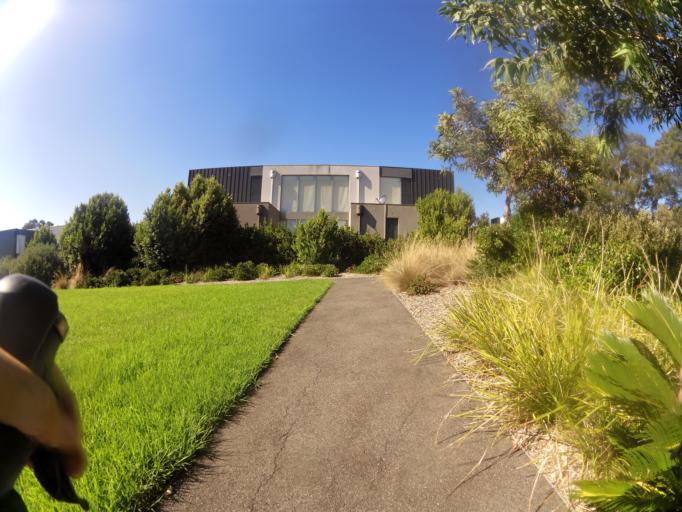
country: AU
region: Victoria
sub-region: Boroondara
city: Kew
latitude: -37.7945
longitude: 145.0263
